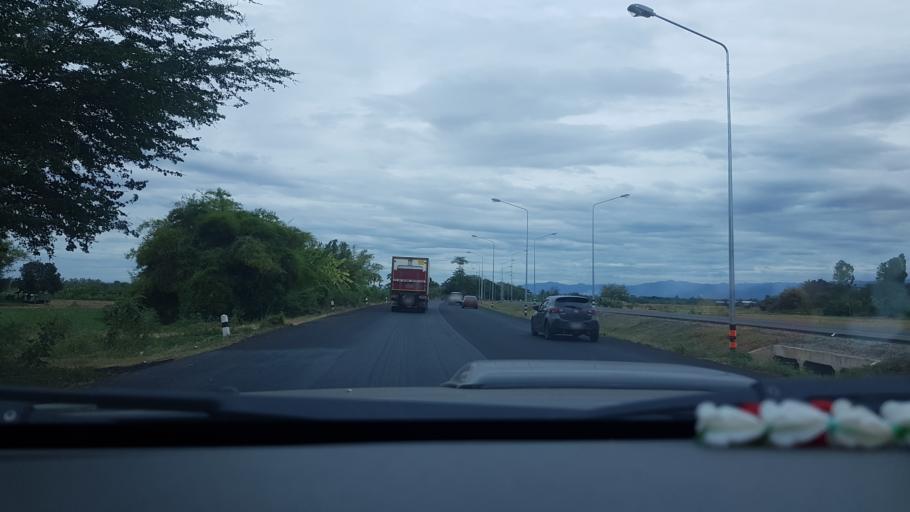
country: TH
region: Phetchabun
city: Phetchabun
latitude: 16.4912
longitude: 101.1420
